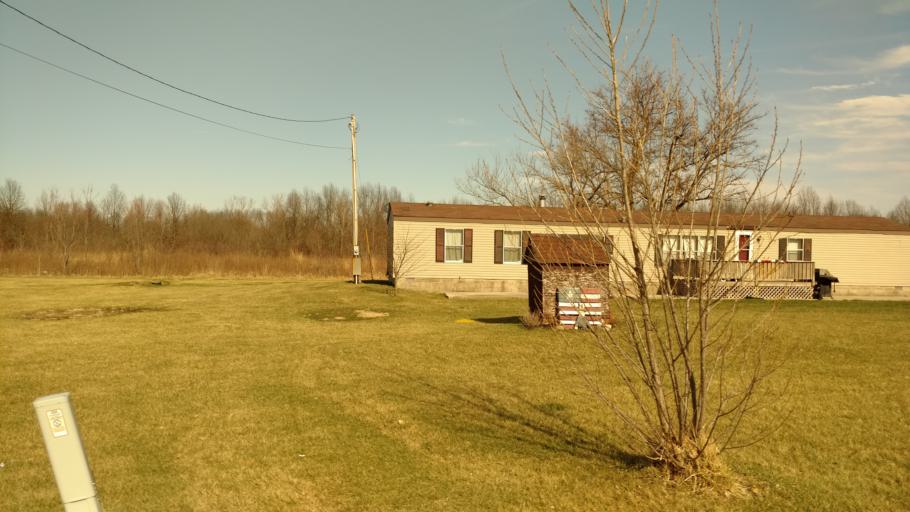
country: US
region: Ohio
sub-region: Hardin County
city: Forest
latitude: 40.6991
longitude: -83.3894
